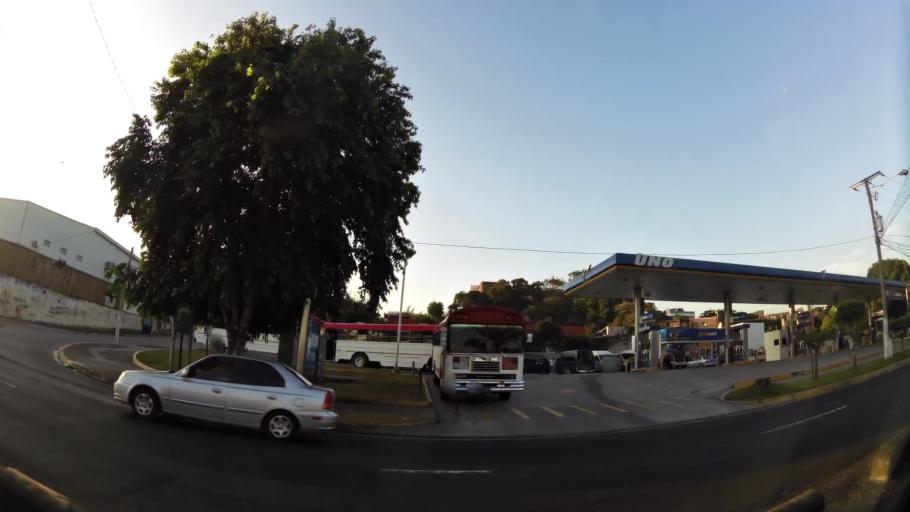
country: SV
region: San Salvador
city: San Salvador
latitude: 13.7042
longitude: -89.2170
